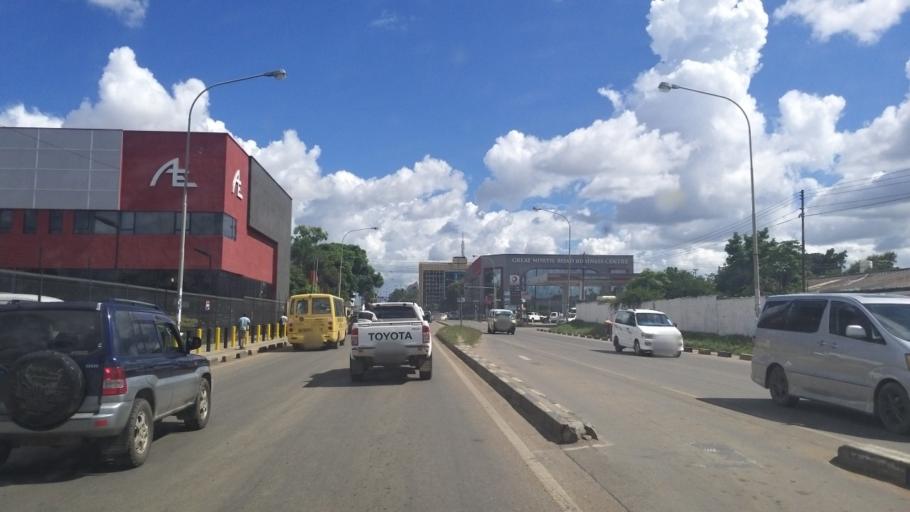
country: ZM
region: Lusaka
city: Lusaka
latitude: -15.4035
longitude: 28.2790
